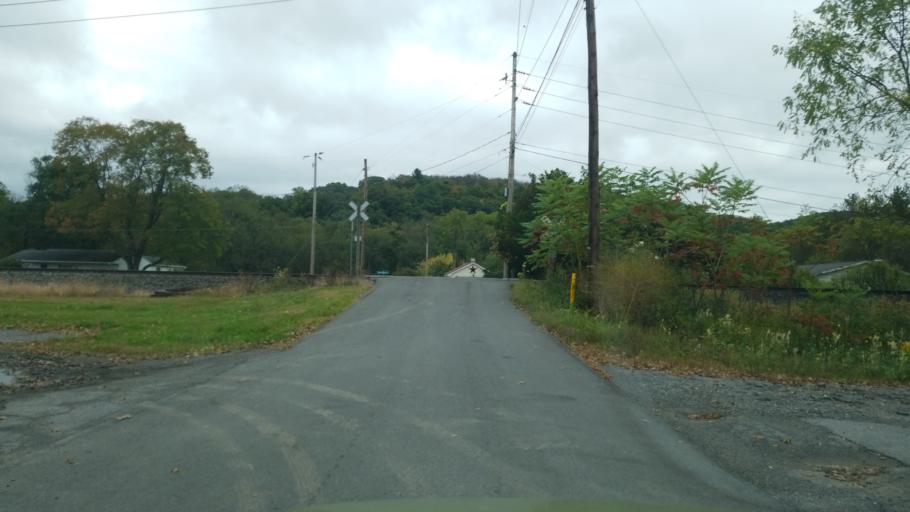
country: US
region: Pennsylvania
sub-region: Clearfield County
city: Hyde
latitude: 40.9969
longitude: -78.4655
